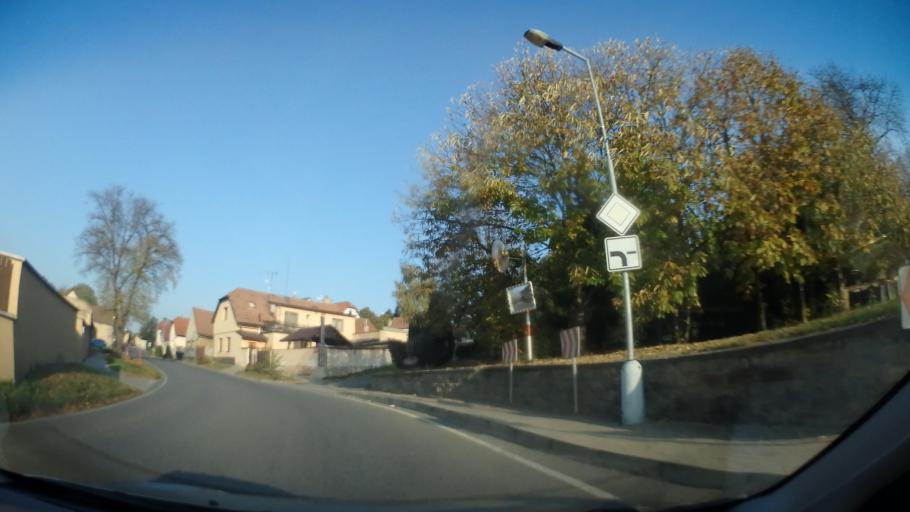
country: CZ
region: Central Bohemia
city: Jirny
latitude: 50.1137
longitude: 14.7025
